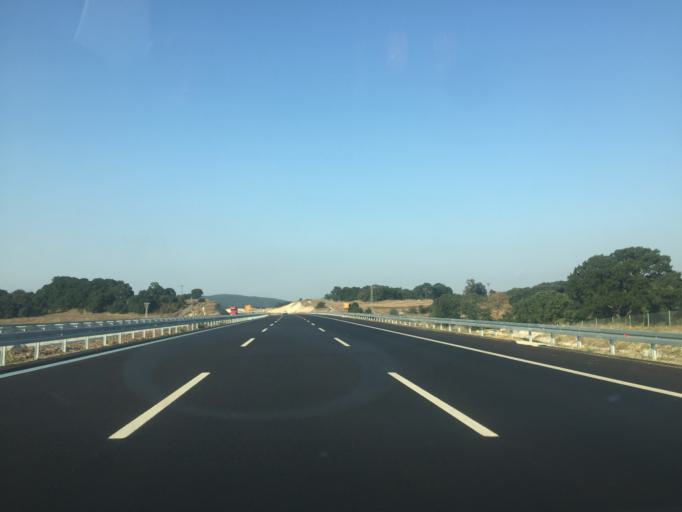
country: TR
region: Balikesir
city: Ertugrul
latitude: 39.4953
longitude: 27.6688
